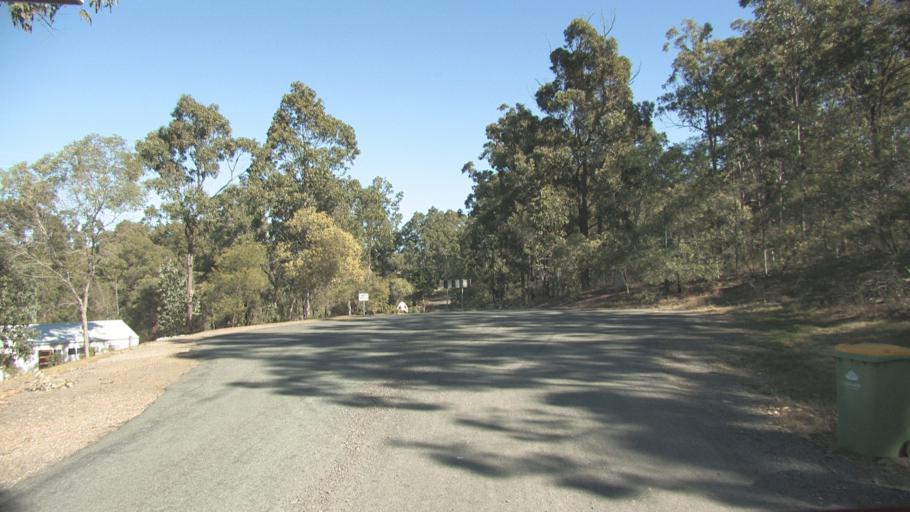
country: AU
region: Queensland
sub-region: Ipswich
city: Springfield Lakes
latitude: -27.7088
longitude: 152.9159
